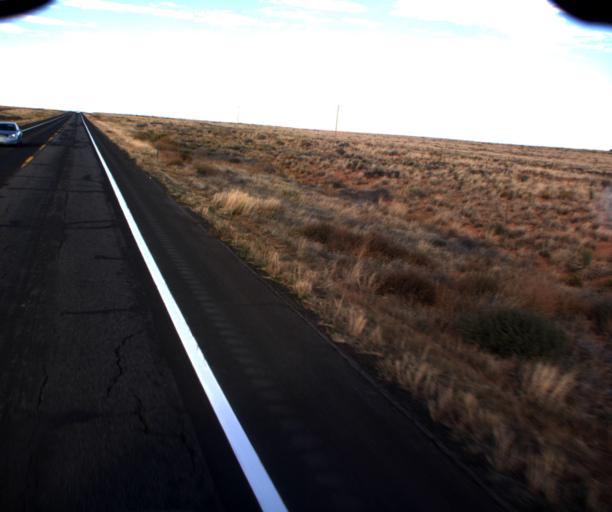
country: US
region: Arizona
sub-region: Apache County
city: Lukachukai
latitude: 36.9586
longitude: -109.3138
